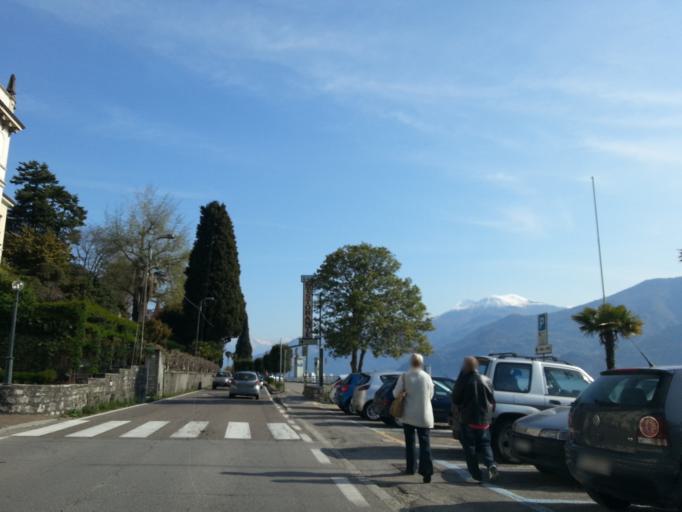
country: IT
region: Lombardy
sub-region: Provincia di Como
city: Cadenabbia
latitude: 45.9892
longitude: 9.2363
